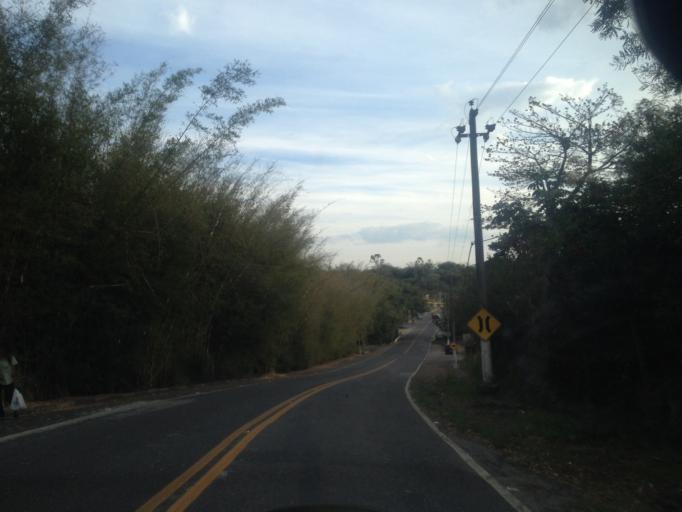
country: BR
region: Rio de Janeiro
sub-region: Quatis
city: Quatis
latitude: -22.4126
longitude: -44.2725
